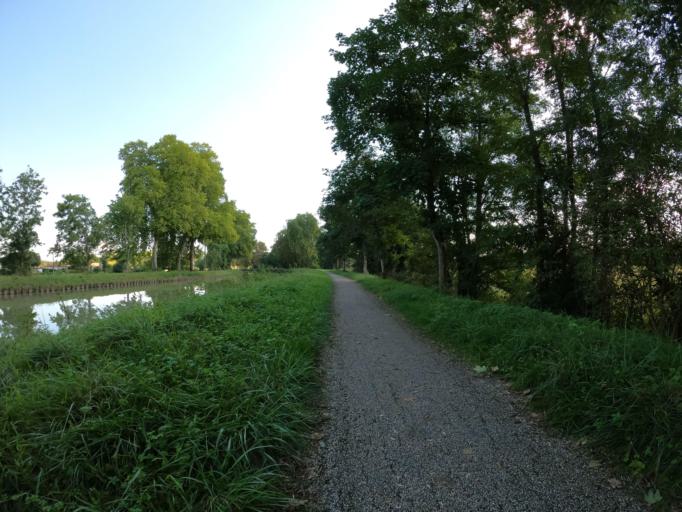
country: FR
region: Midi-Pyrenees
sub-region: Departement du Tarn-et-Garonne
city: Lamagistere
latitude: 44.1184
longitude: 0.8496
